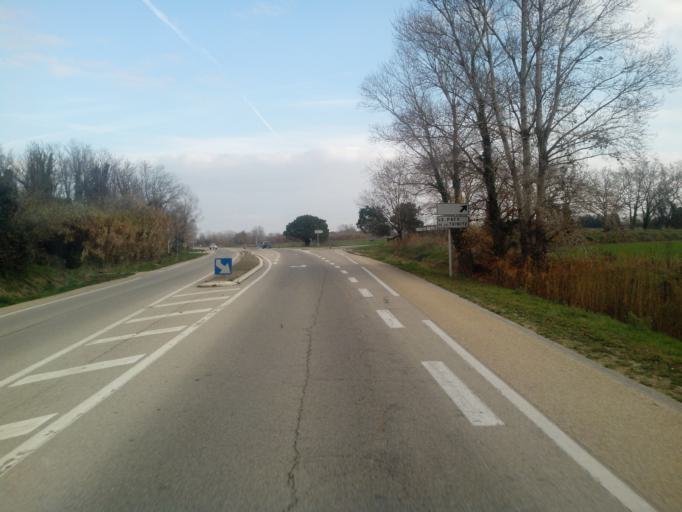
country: FR
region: Languedoc-Roussillon
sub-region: Departement du Gard
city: Saint-Gilles
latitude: 43.5821
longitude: 4.4475
